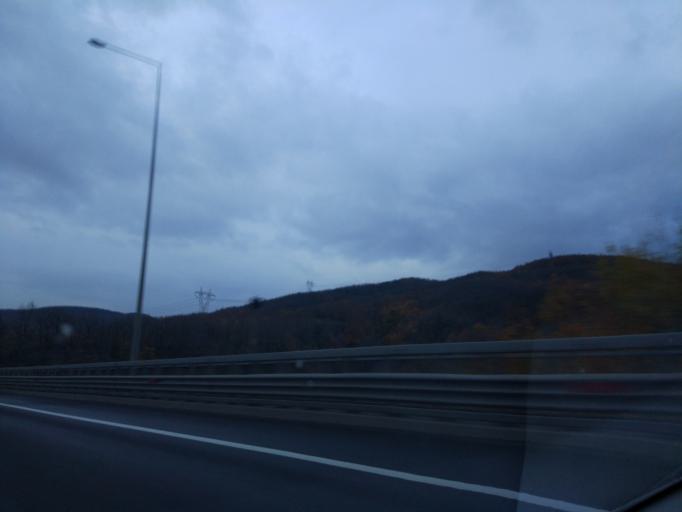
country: TR
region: Duzce
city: Kaynasli
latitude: 40.7773
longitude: 31.3536
